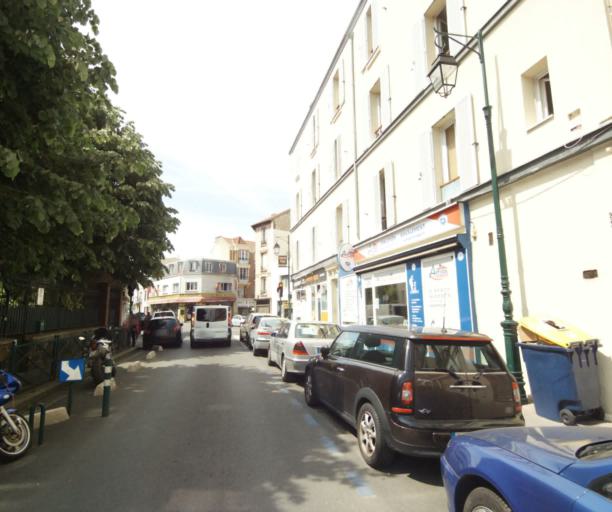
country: FR
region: Ile-de-France
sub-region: Departement des Hauts-de-Seine
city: Colombes
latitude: 48.9212
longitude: 2.2591
